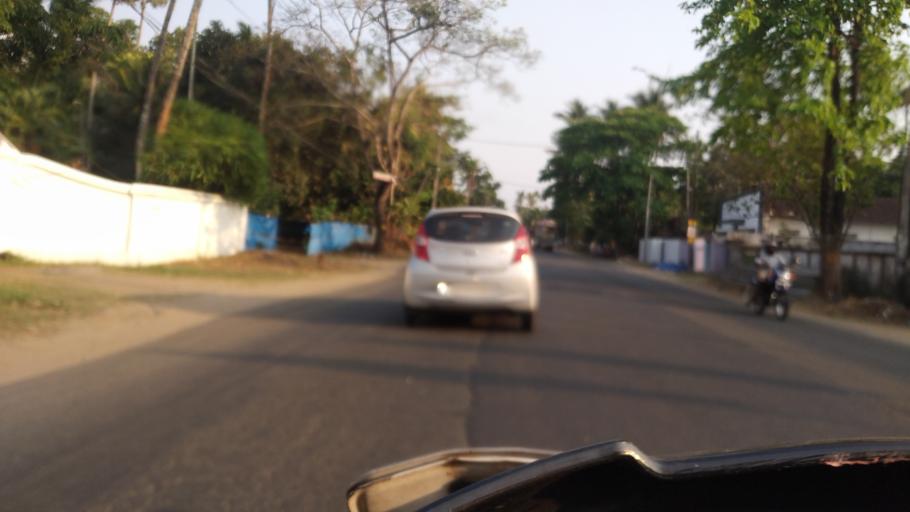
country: IN
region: Kerala
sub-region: Thrissur District
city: Thanniyam
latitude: 10.3786
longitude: 76.1222
